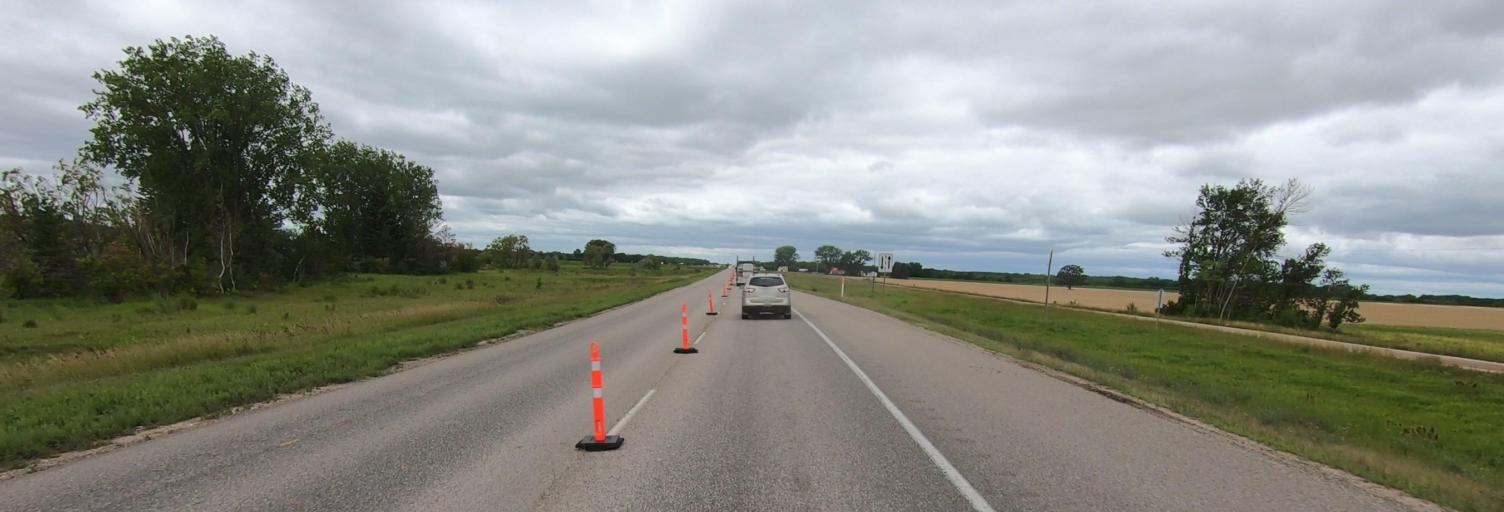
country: CA
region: Manitoba
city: Portage la Prairie
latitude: 49.9727
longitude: -98.1057
